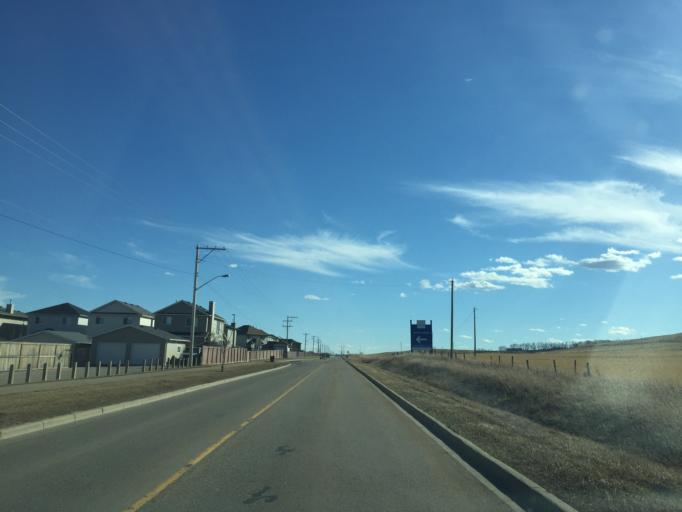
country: CA
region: Alberta
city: Airdrie
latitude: 51.2893
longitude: -114.0486
